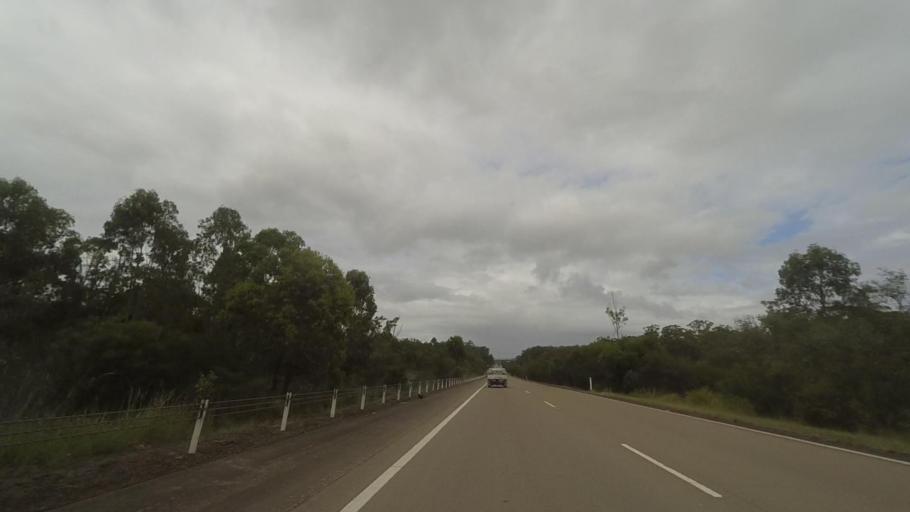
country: AU
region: New South Wales
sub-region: Port Stephens Shire
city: Medowie
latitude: -32.6361
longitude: 151.9348
